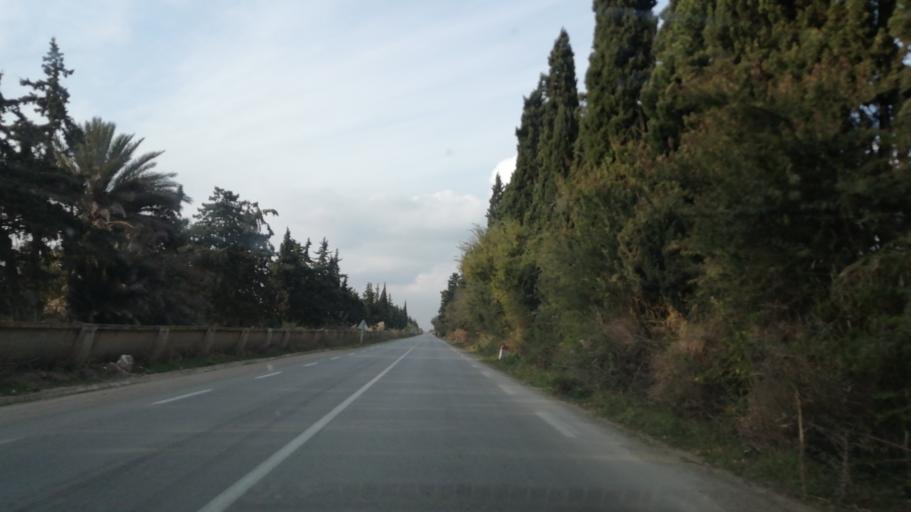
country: DZ
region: Mascara
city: Sig
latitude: 35.6320
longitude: 0.0395
